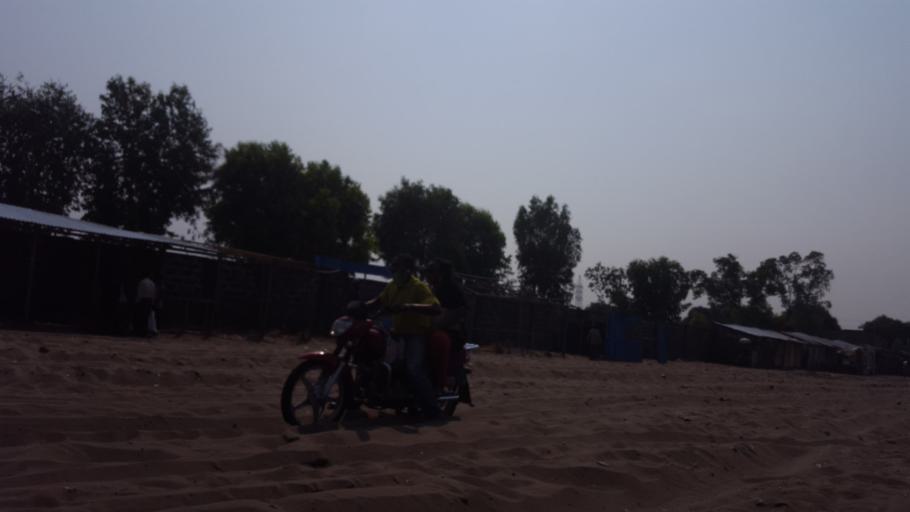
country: CD
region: Kinshasa
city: Masina
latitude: -4.3583
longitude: 15.5058
